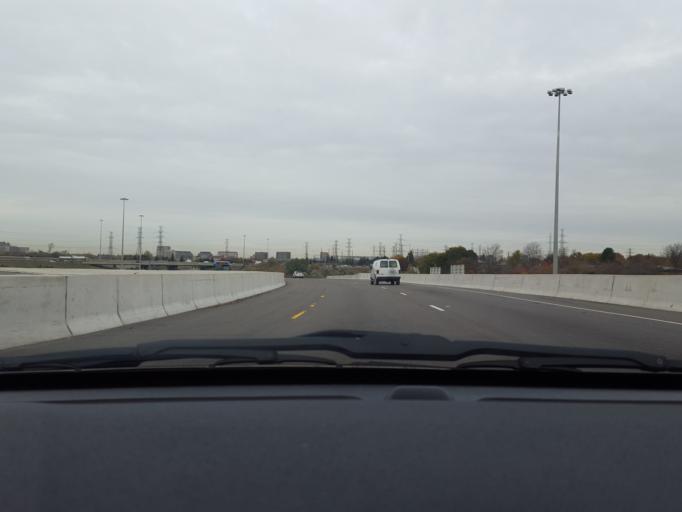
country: CA
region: Ontario
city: Etobicoke
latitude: 43.6726
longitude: -79.5733
